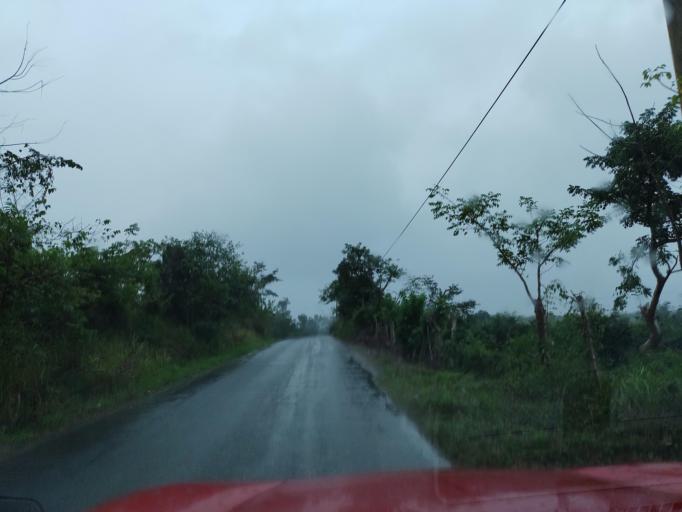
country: MX
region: Veracruz
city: Agua Dulce
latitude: 20.3366
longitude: -97.3127
